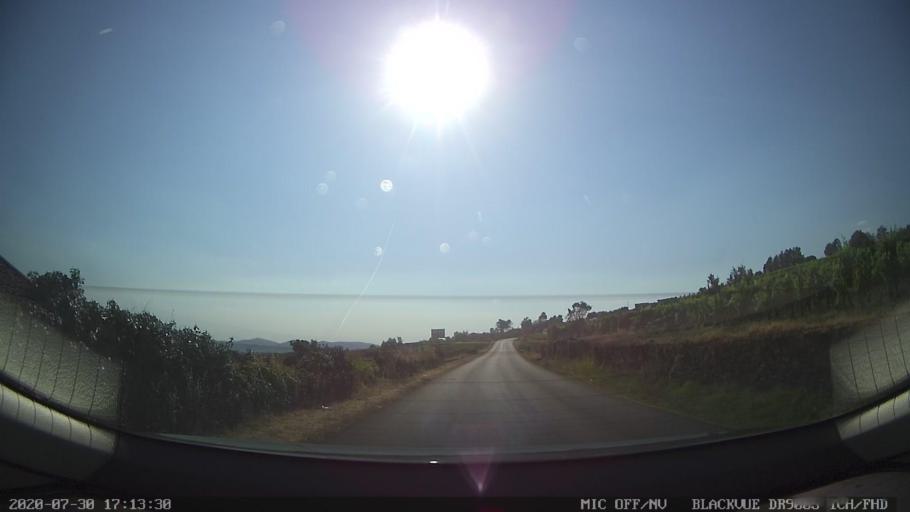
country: PT
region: Vila Real
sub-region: Sabrosa
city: Sabrosa
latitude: 41.2640
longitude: -7.4872
